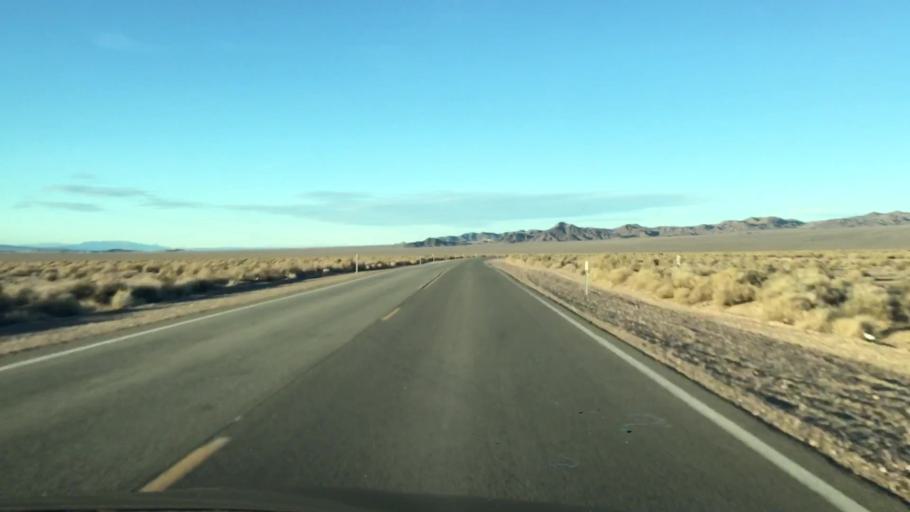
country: US
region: California
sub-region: San Bernardino County
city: Fort Irwin
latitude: 35.3101
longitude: -116.0839
